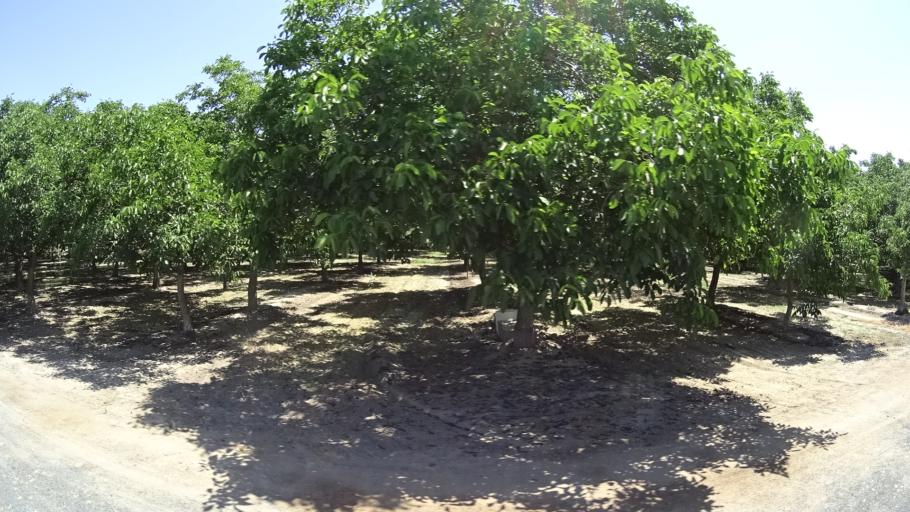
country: US
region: California
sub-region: Fresno County
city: Laton
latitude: 36.4176
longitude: -119.6727
